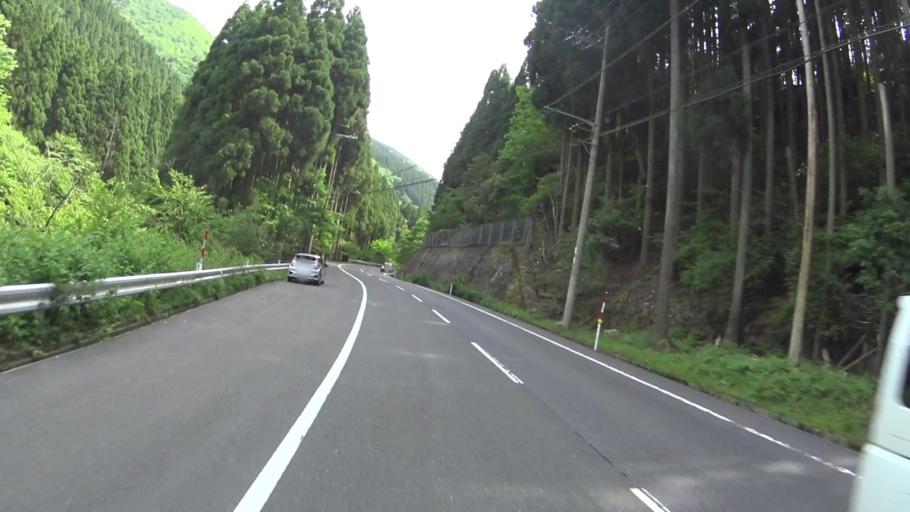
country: JP
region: Shiga Prefecture
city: Kitahama
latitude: 35.2206
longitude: 135.8620
